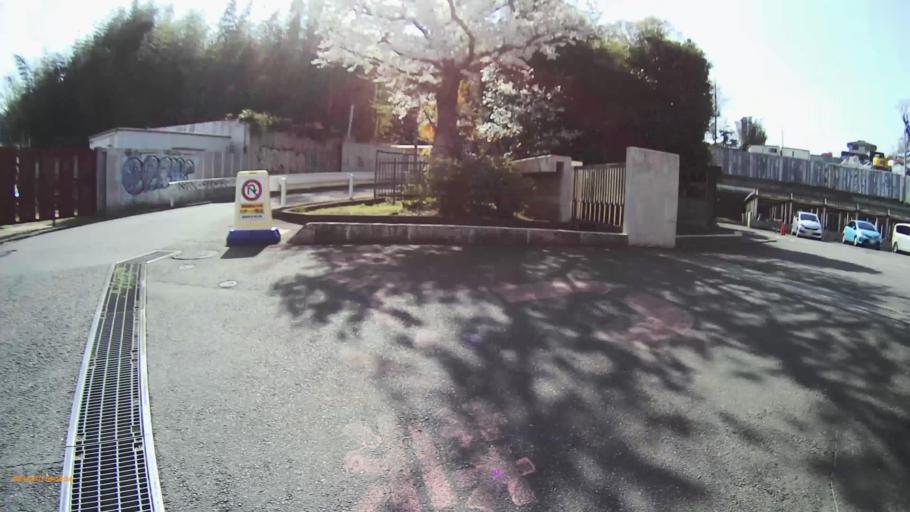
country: JP
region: Kanagawa
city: Atsugi
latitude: 35.4362
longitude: 139.4135
